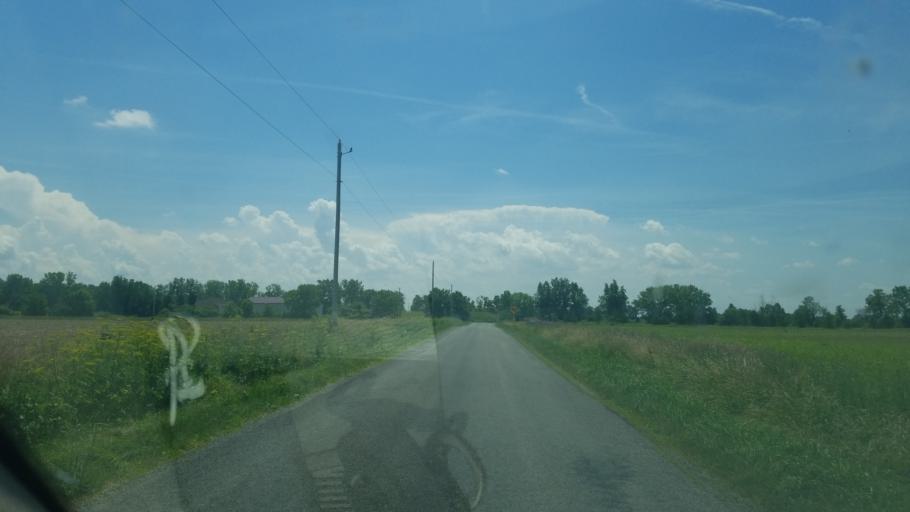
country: US
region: Ohio
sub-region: Hancock County
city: Findlay
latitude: 40.9954
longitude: -83.6362
